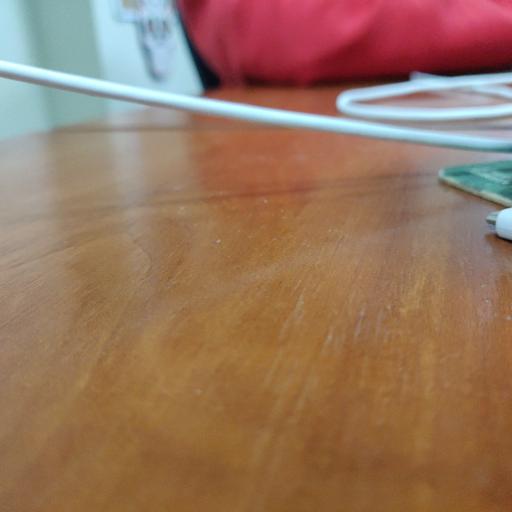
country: LV
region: Jelgava
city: Jelgava
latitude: 56.6944
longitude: 23.6809
